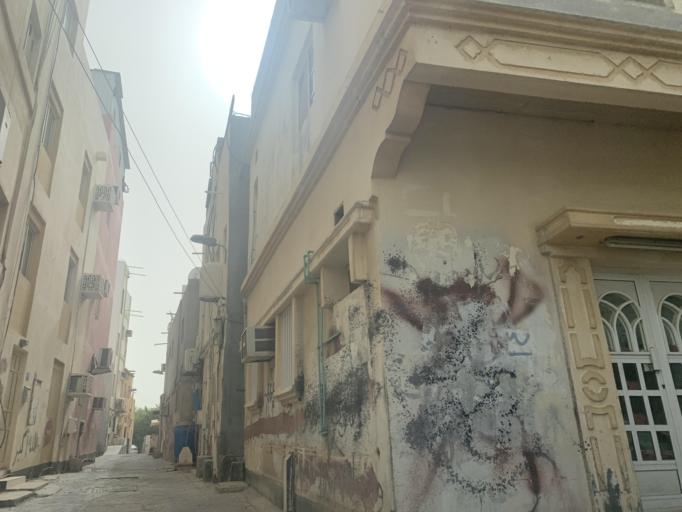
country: BH
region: Manama
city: Jidd Hafs
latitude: 26.2241
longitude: 50.5577
